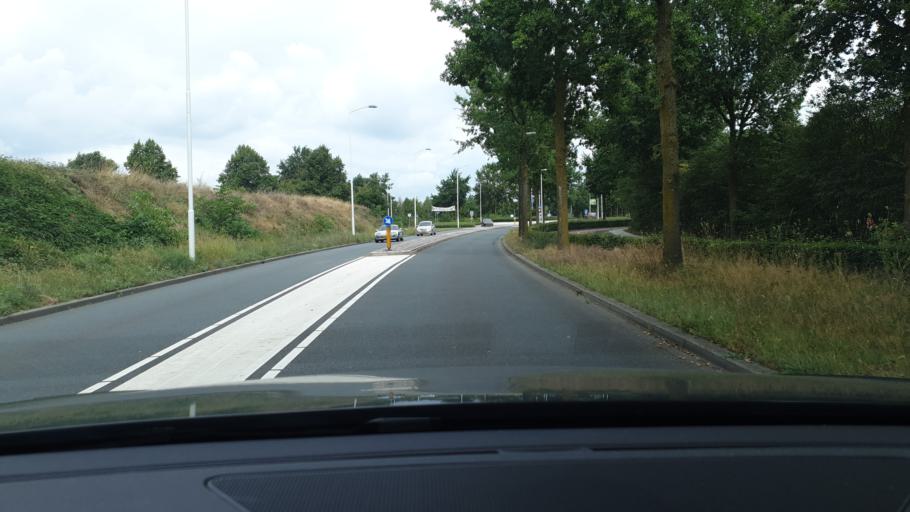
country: NL
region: North Brabant
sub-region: Gemeente Best
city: Best
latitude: 51.5027
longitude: 5.3789
